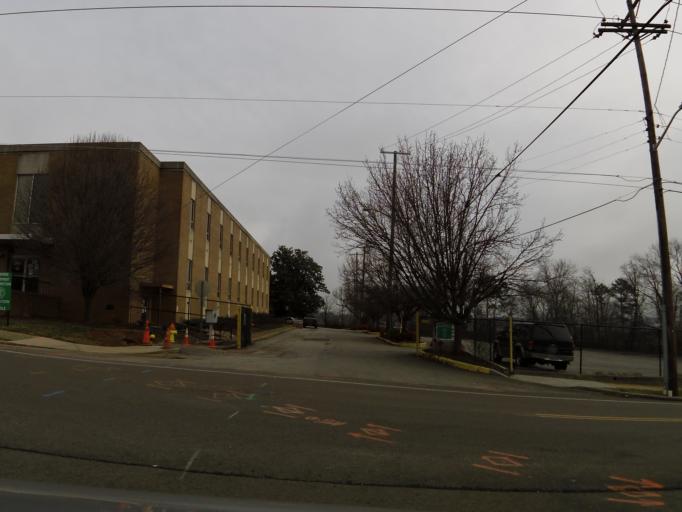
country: US
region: Tennessee
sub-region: Knox County
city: Knoxville
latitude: 35.9790
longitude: -83.9387
